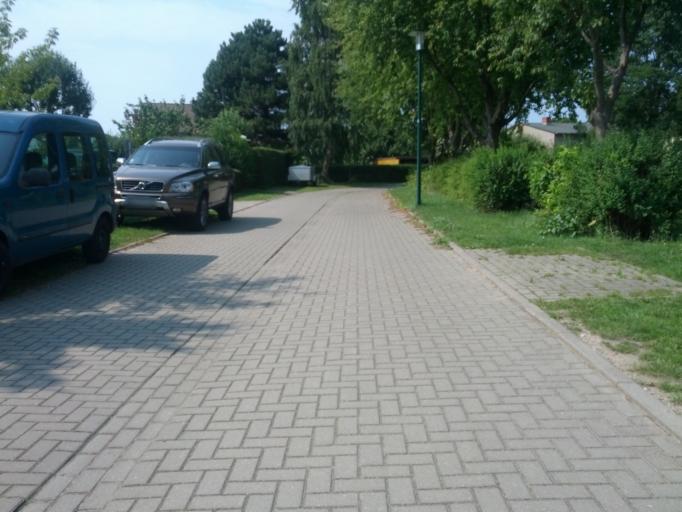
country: DE
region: Mecklenburg-Vorpommern
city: Bastorf
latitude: 54.1010
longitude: 11.6203
